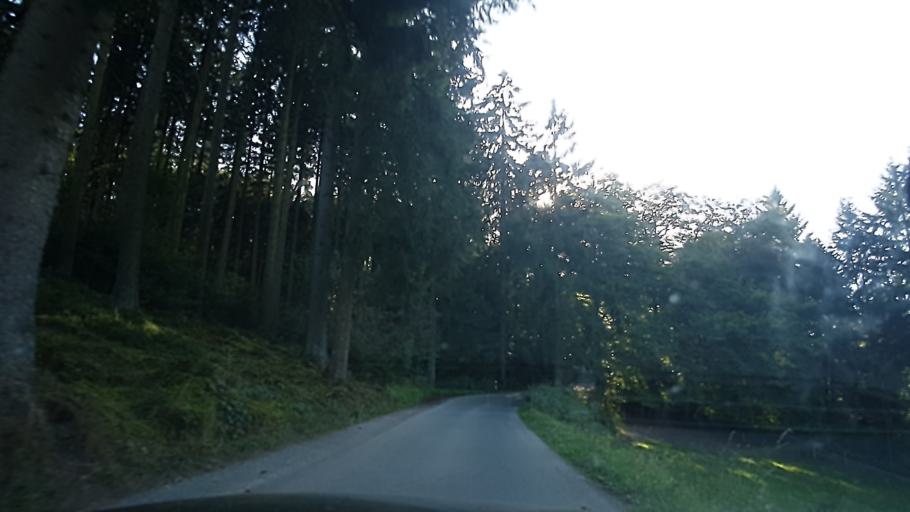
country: DE
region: North Rhine-Westphalia
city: Halver
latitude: 51.1342
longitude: 7.4852
